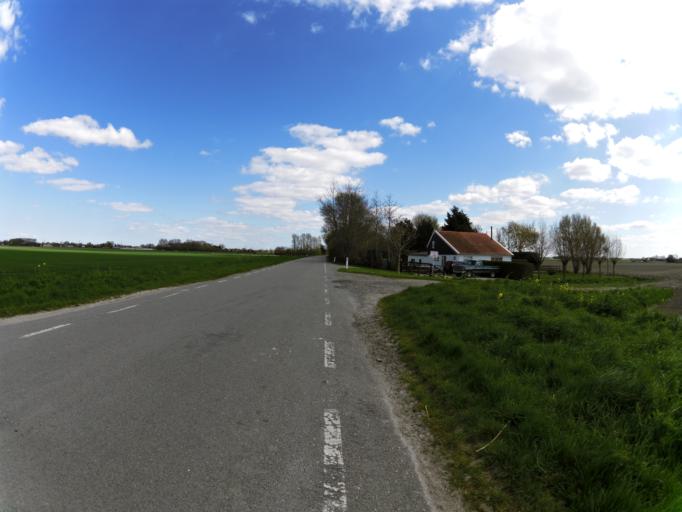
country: NL
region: South Holland
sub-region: Gemeente Hellevoetsluis
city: Nieuwenhoorn
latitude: 51.8804
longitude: 4.1143
